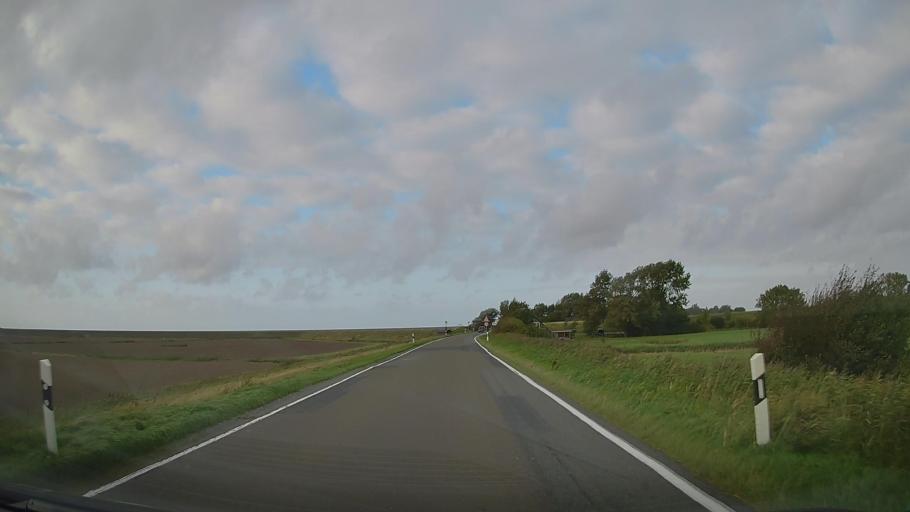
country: DE
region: Schleswig-Holstein
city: Osterhever
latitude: 54.3896
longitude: 8.7579
